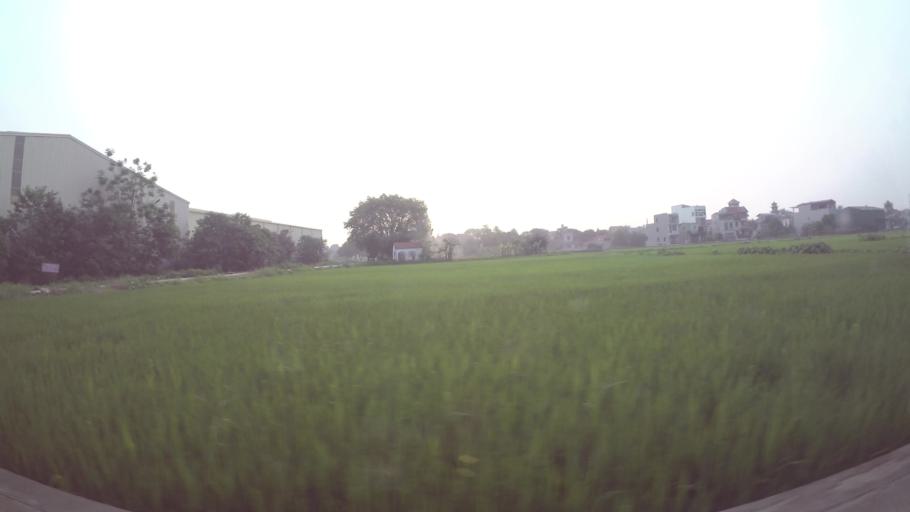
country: VN
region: Ha Noi
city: Thuong Tin
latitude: 20.8740
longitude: 105.8702
